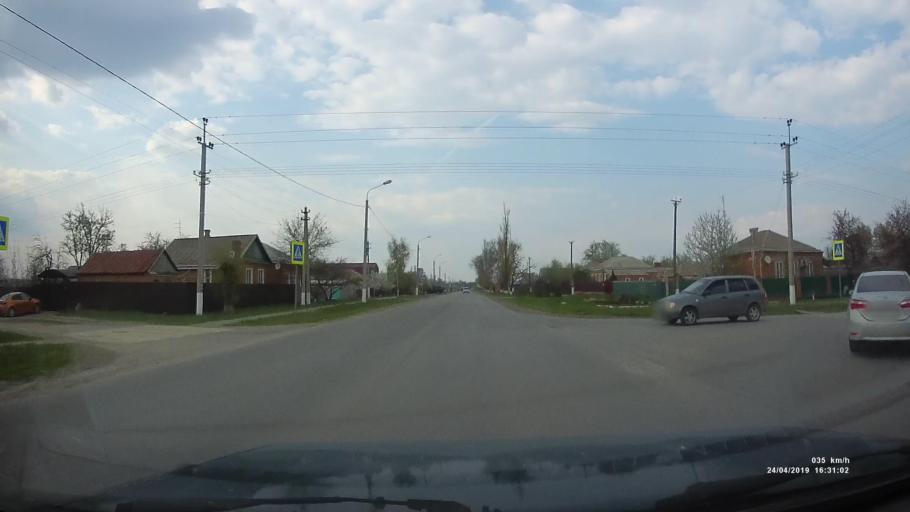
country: RU
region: Rostov
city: Orlovskiy
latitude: 46.8781
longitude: 42.0384
